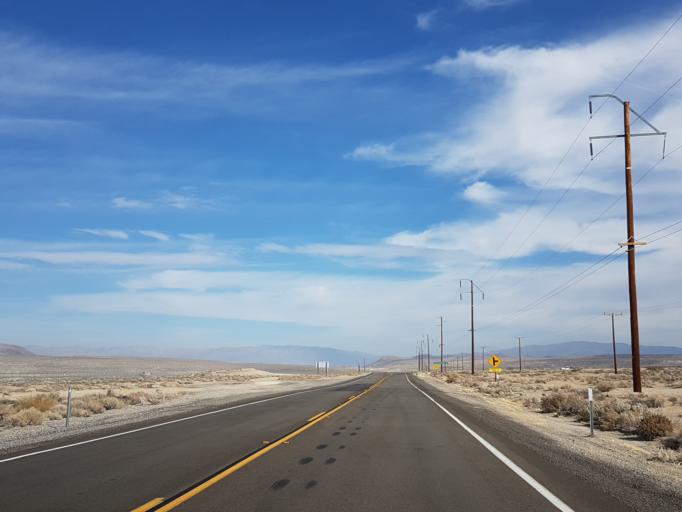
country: US
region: California
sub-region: Kern County
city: Ridgecrest
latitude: 35.6467
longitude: -117.5134
